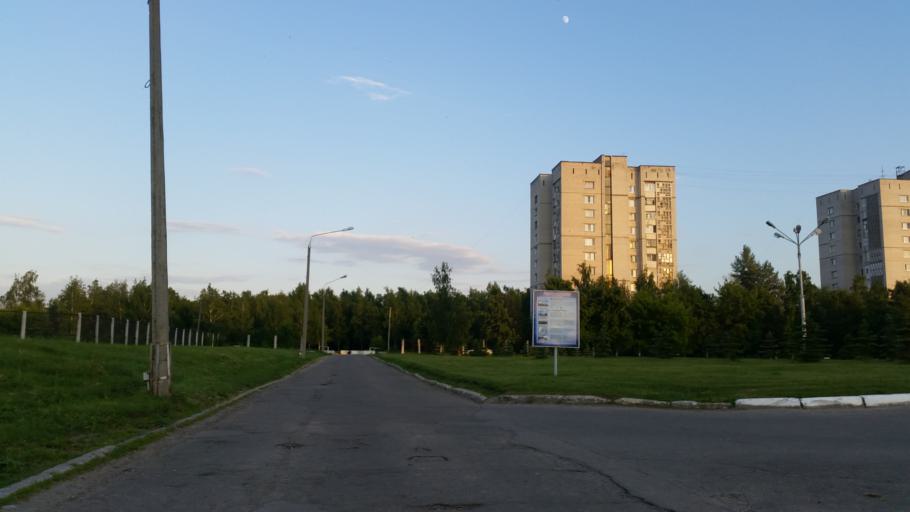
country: RU
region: Ulyanovsk
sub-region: Ulyanovskiy Rayon
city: Ulyanovsk
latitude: 54.3510
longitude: 48.3916
